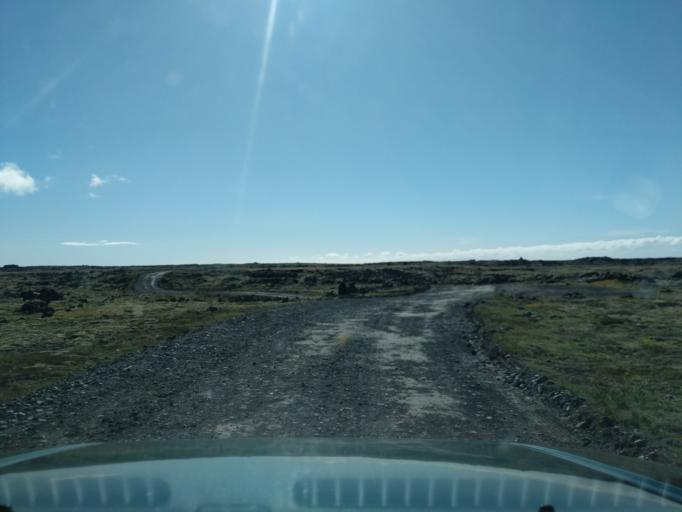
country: IS
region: West
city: Olafsvik
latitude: 64.8734
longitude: -24.0206
